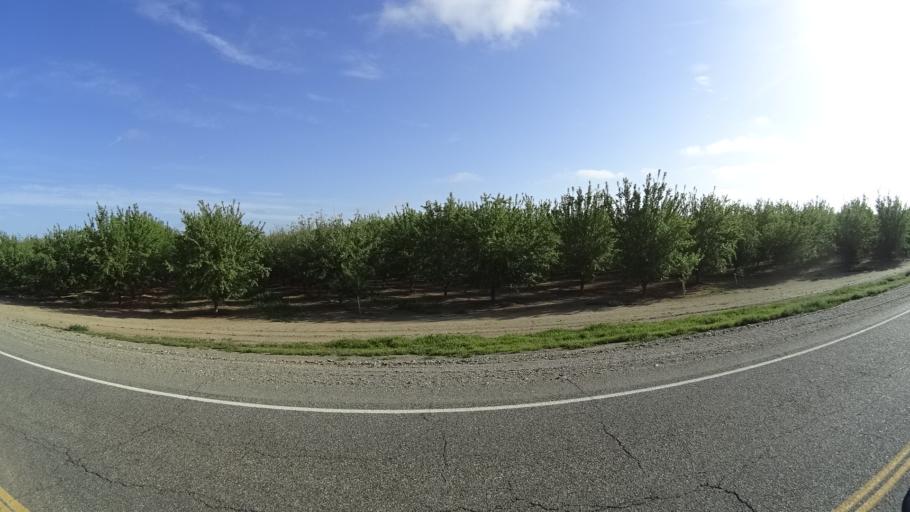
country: US
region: California
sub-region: Glenn County
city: Willows
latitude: 39.5834
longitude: -122.1871
